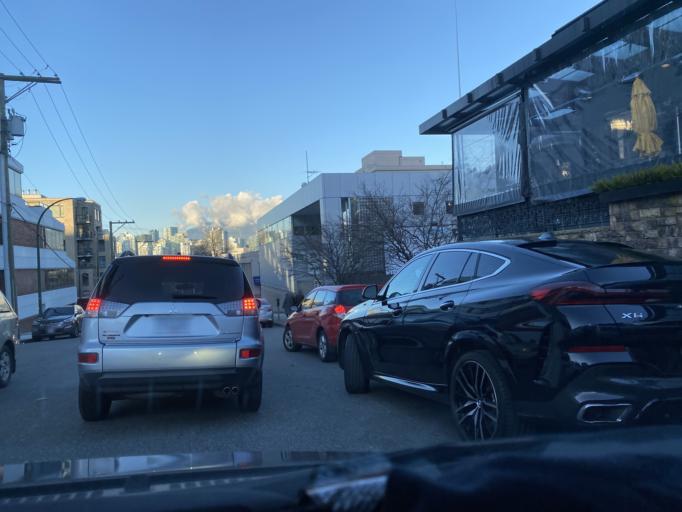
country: CA
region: British Columbia
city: Vancouver
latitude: 49.2635
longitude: -123.1175
